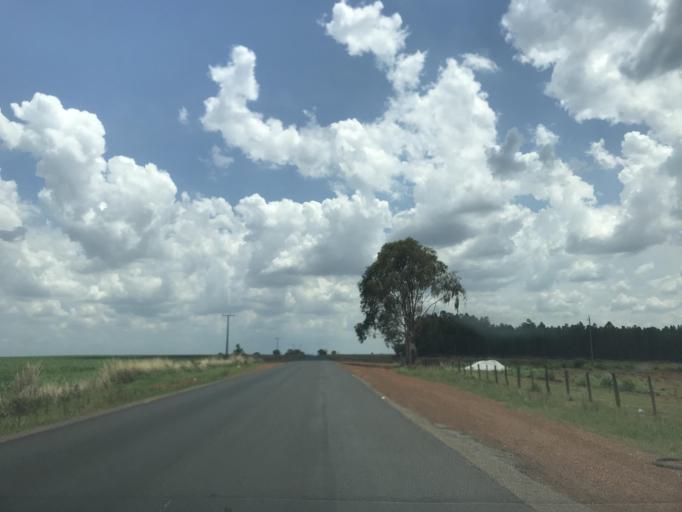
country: BR
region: Goias
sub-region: Piracanjuba
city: Piracanjuba
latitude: -17.3661
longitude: -48.7963
